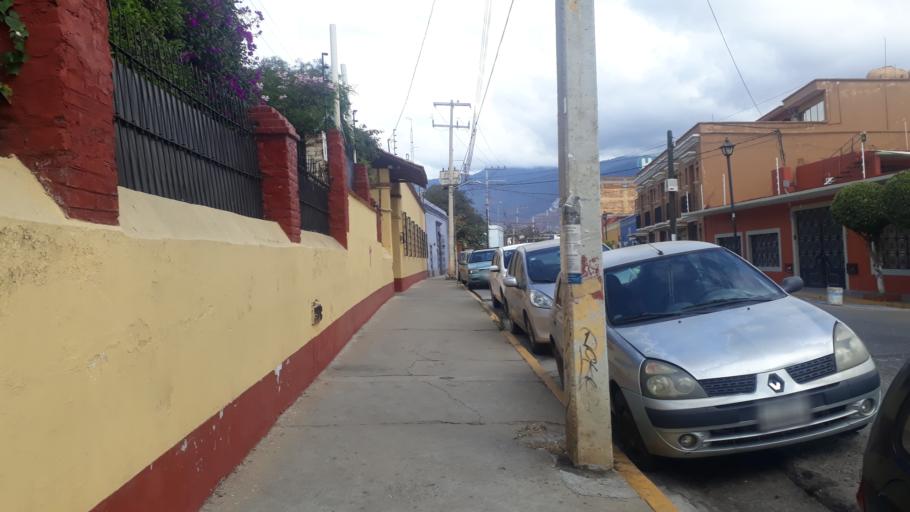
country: MX
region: Oaxaca
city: Oaxaca de Juarez
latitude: 17.0703
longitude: -96.7231
